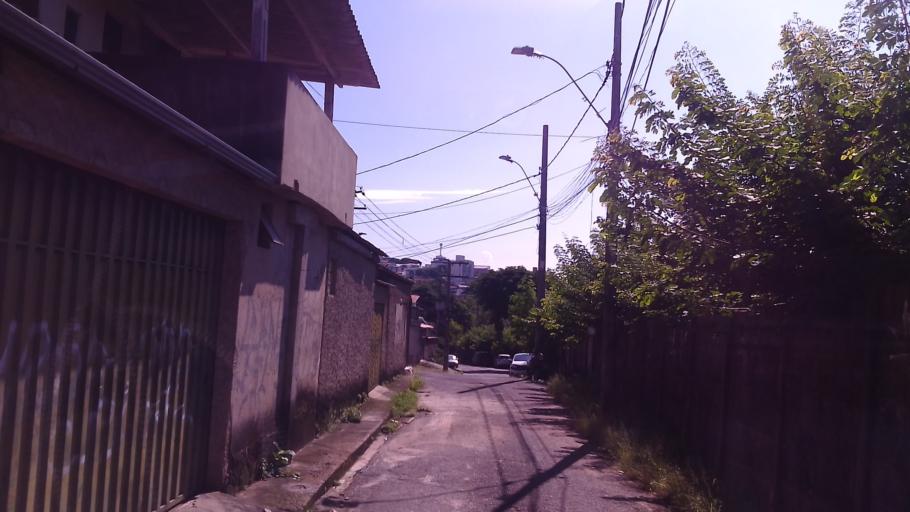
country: BR
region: Minas Gerais
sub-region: Belo Horizonte
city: Belo Horizonte
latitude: -19.8992
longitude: -43.9106
